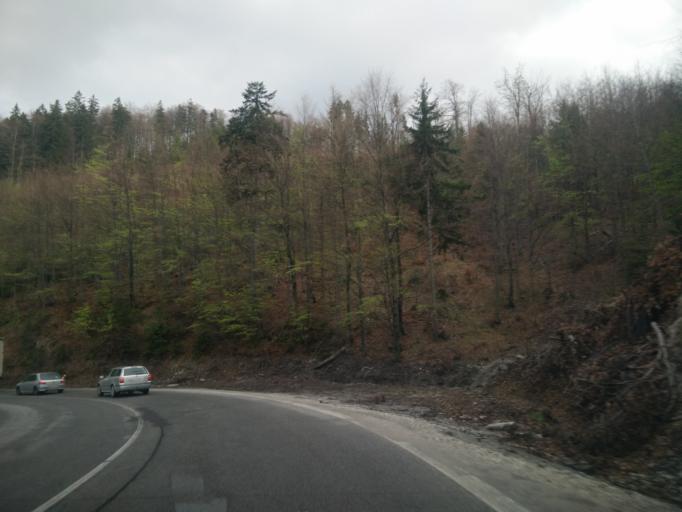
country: SK
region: Banskobystricky
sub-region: Okres Ziar nad Hronom
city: Kremnica
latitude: 48.8373
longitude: 19.0008
